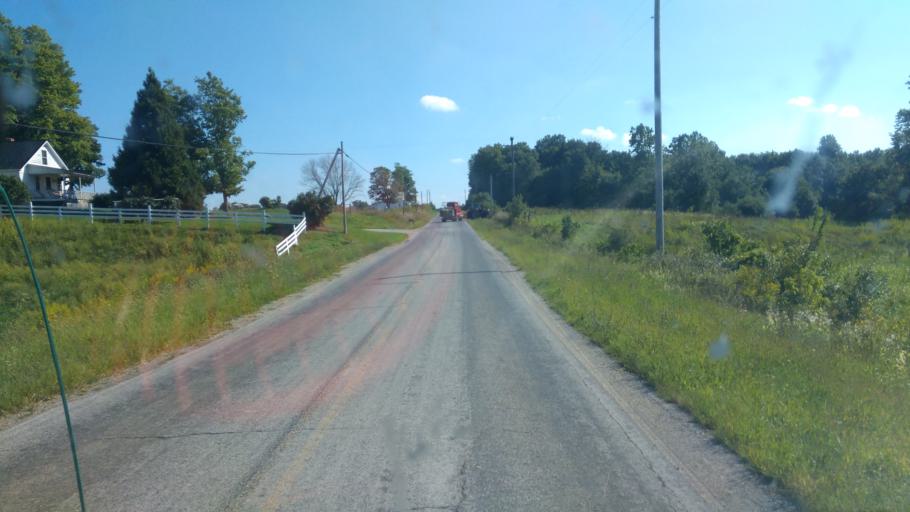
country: US
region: Ohio
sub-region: Ashland County
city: Ashland
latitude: 40.9080
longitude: -82.4359
